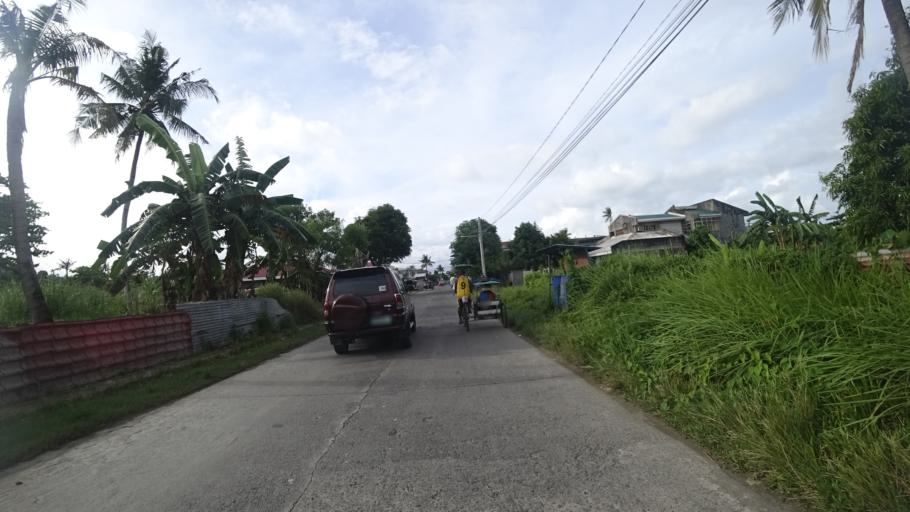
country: PH
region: Eastern Visayas
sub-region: Province of Leyte
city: Panalanoy
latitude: 11.2299
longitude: 125.0039
